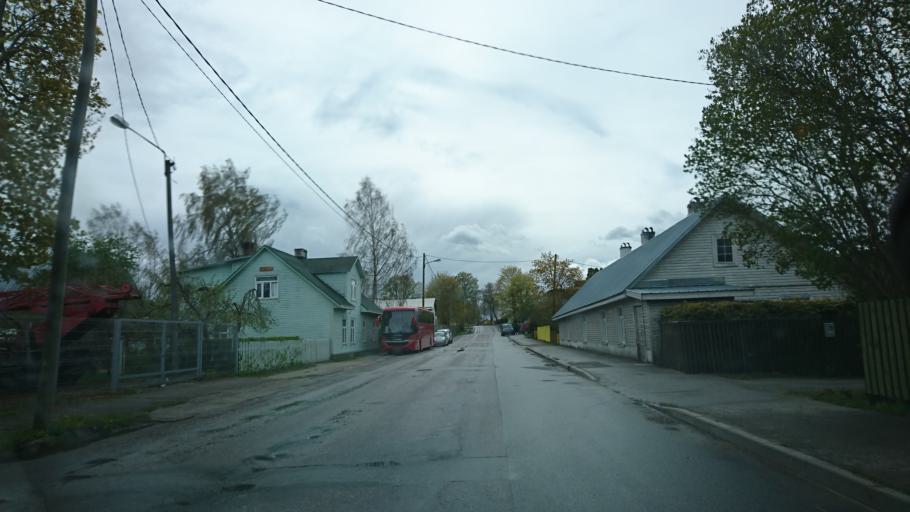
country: EE
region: Laeaene-Virumaa
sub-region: Rakvere linn
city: Rakvere
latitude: 59.3360
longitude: 26.3604
